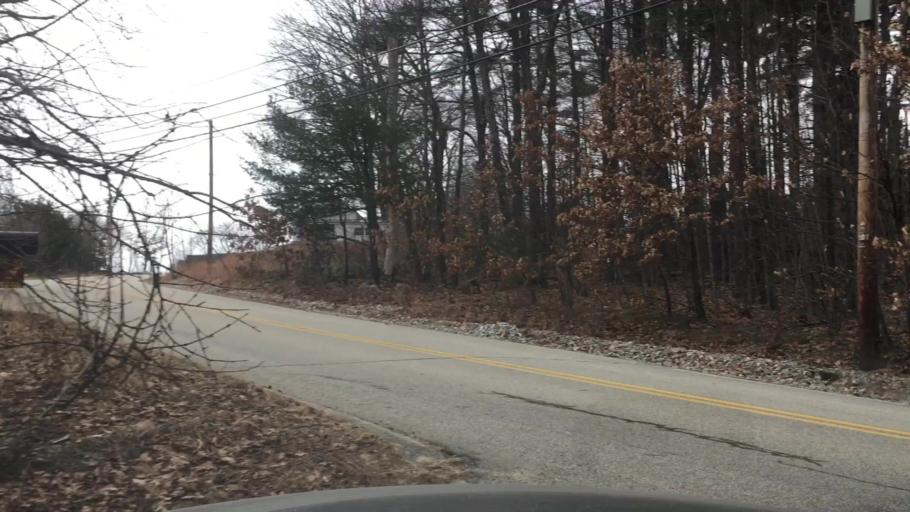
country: US
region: New Hampshire
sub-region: Hillsborough County
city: Mont Vernon
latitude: 42.9219
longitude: -71.6024
